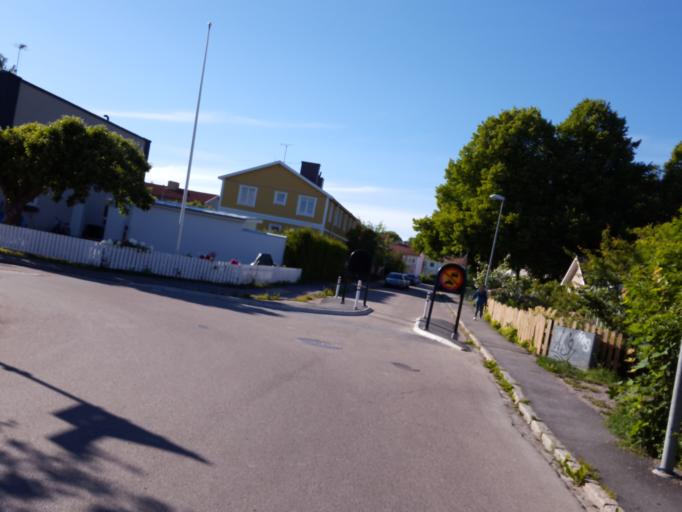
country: SE
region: Uppsala
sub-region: Uppsala Kommun
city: Uppsala
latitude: 59.8621
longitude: 17.6615
